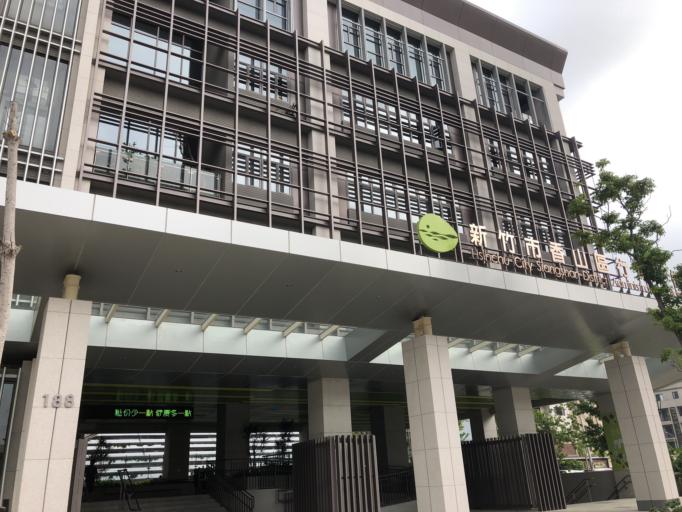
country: TW
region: Taiwan
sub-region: Hsinchu
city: Hsinchu
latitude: 24.7940
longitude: 120.9425
